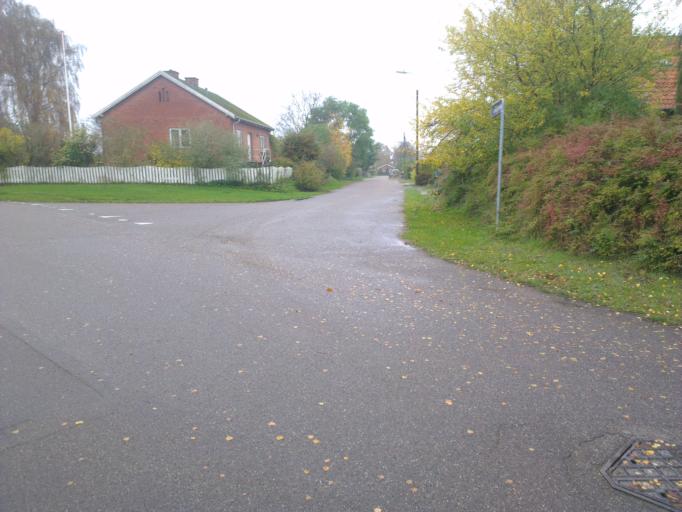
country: DK
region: Capital Region
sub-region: Frederikssund Kommune
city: Jaegerspris
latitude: 55.8543
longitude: 11.9922
